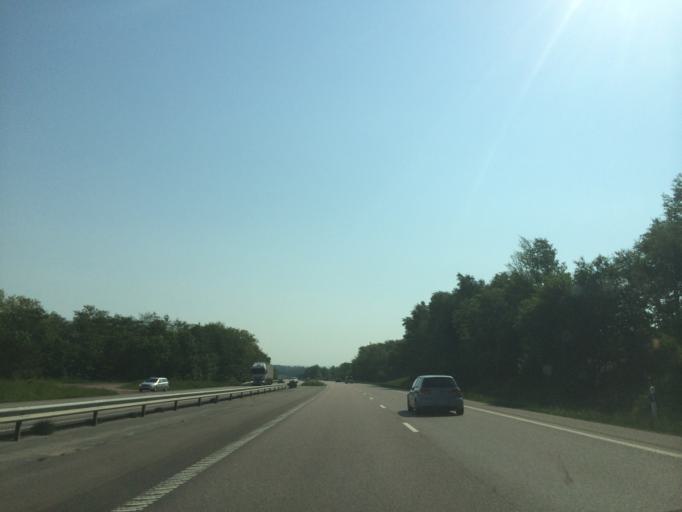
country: SE
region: Skane
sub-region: Helsingborg
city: Hyllinge
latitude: 56.0878
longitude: 12.7931
